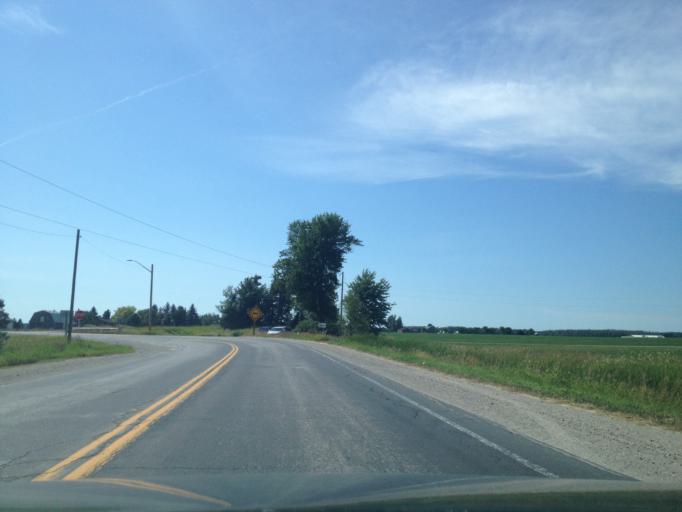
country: CA
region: Ontario
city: Stratford
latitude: 43.5027
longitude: -80.8802
